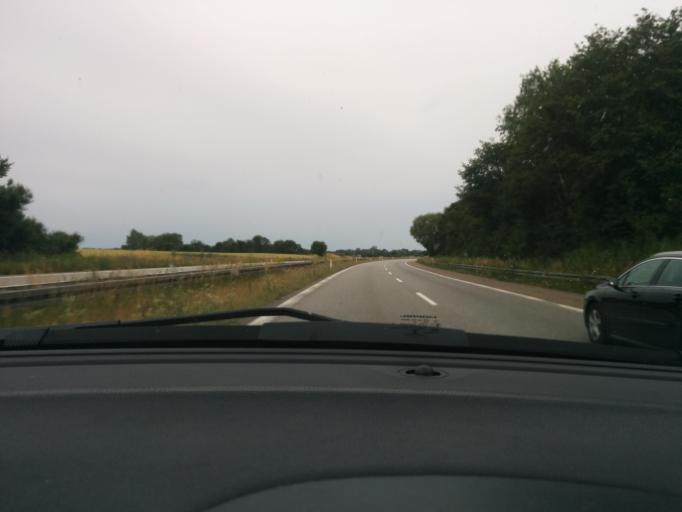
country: DK
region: Zealand
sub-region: Faxe Kommune
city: Ronnede
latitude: 55.3489
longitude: 12.0645
